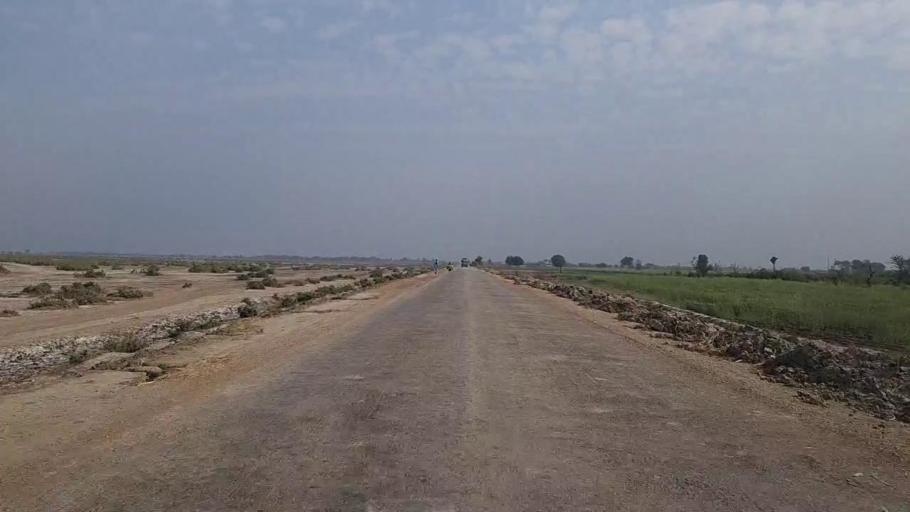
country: PK
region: Sindh
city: Mirwah Gorchani
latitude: 25.4095
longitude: 69.0412
